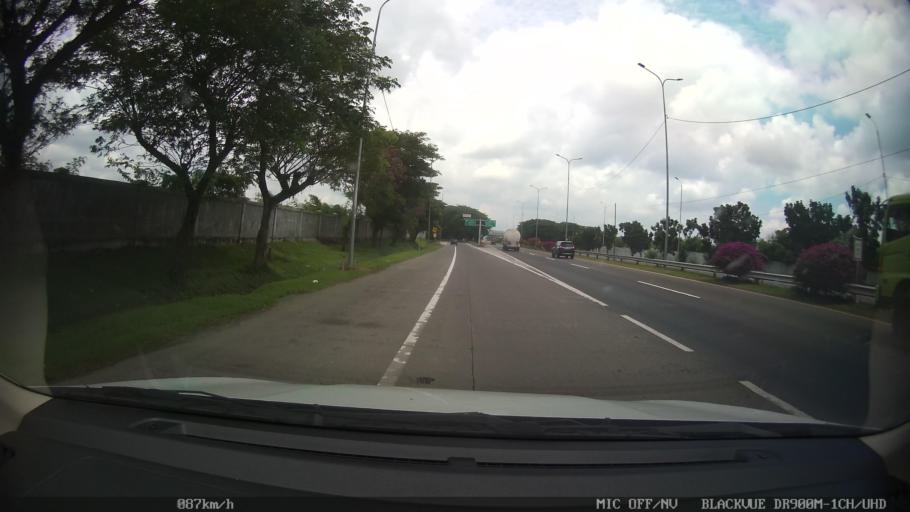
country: ID
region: North Sumatra
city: Medan
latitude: 3.6345
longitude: 98.7116
